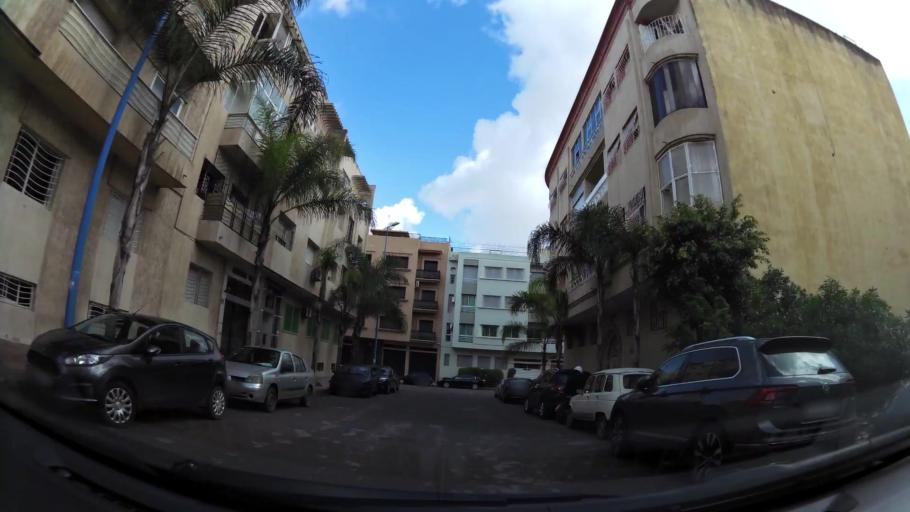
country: MA
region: Grand Casablanca
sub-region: Casablanca
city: Casablanca
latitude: 33.5552
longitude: -7.6260
